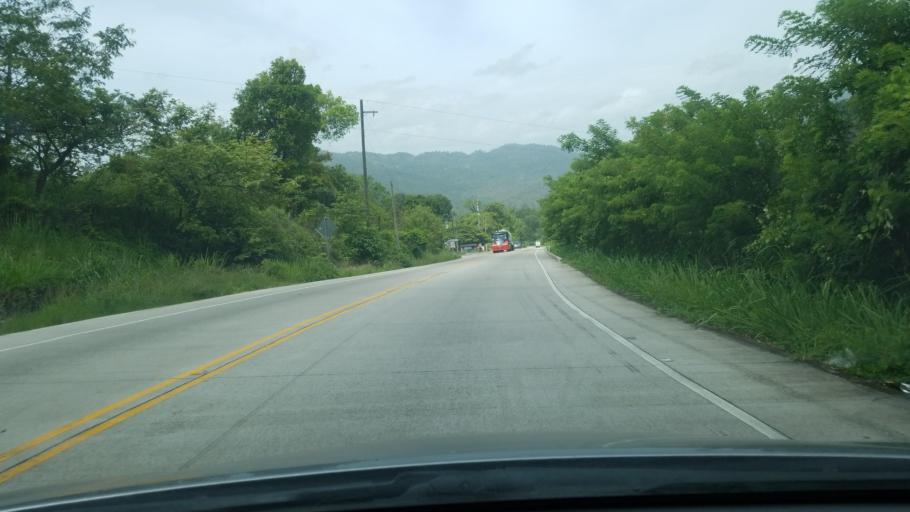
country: HN
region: Copan
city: Quezailica
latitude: 14.9087
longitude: -88.7520
